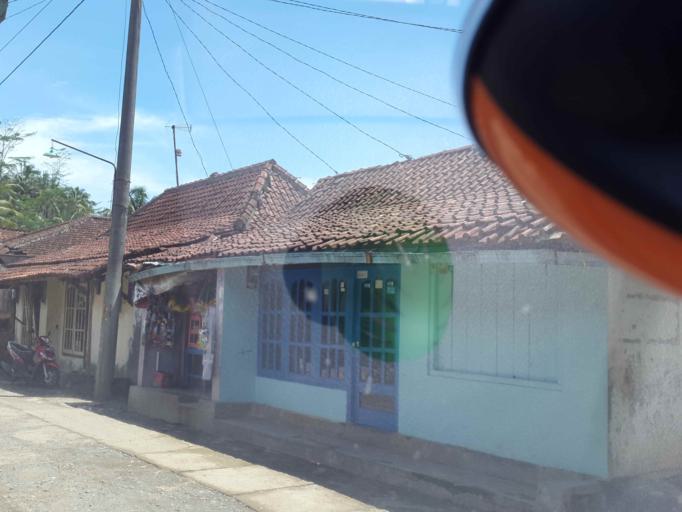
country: ID
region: Central Java
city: Purbalingga
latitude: -7.3626
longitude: 109.6217
